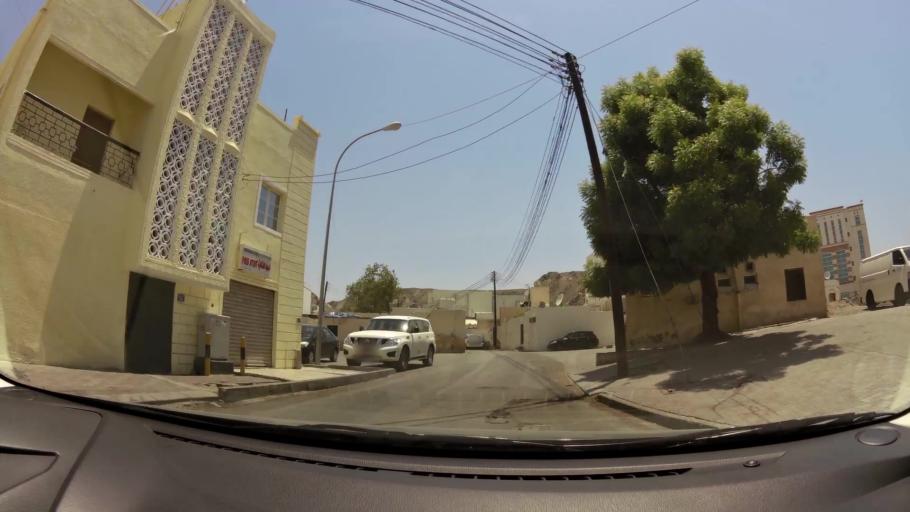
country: OM
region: Muhafazat Masqat
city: Muscat
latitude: 23.6216
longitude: 58.5550
